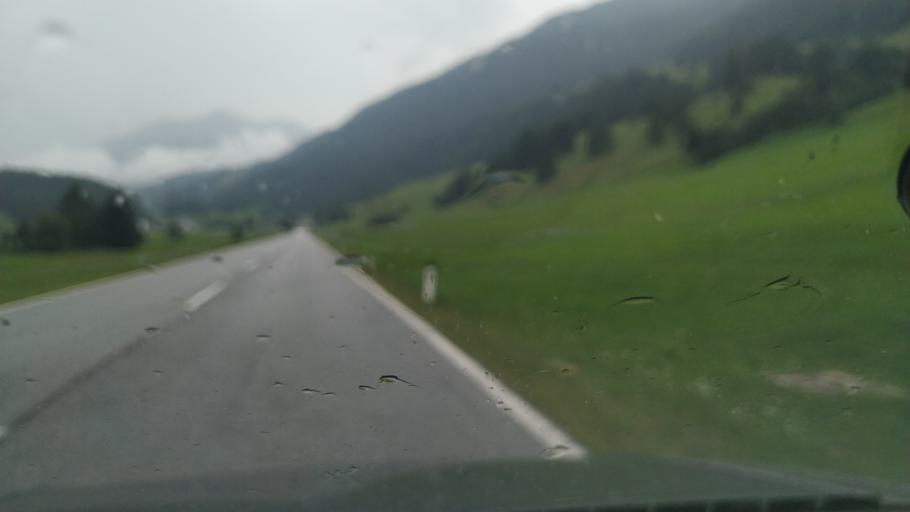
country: AT
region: Tyrol
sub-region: Politischer Bezirk Landeck
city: Nauders
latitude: 46.8585
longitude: 10.5069
